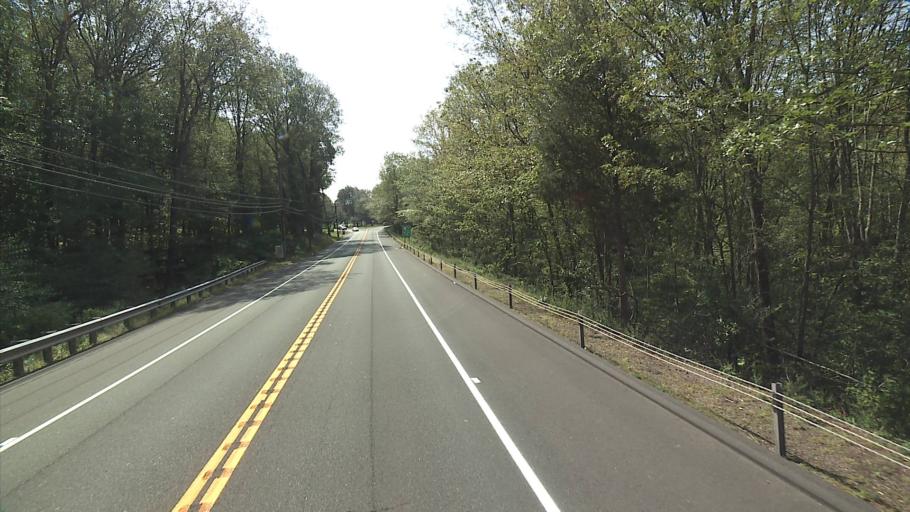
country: US
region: Connecticut
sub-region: New Haven County
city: Guilford
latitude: 41.3621
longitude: -72.6381
